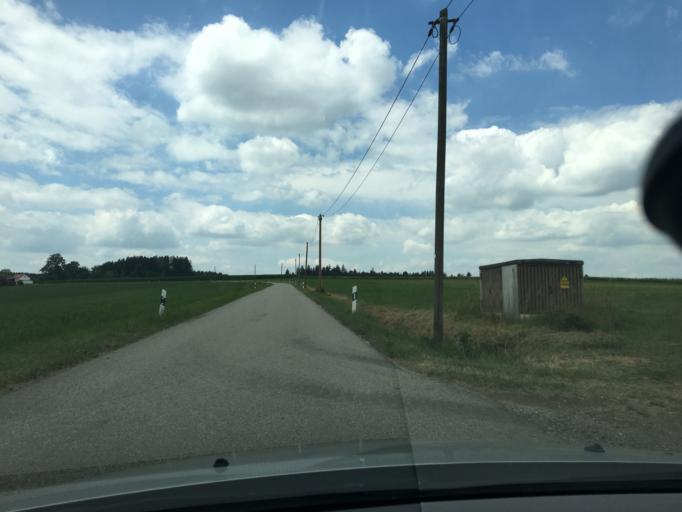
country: DE
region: Bavaria
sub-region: Upper Bavaria
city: Egglkofen
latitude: 48.3932
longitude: 12.4845
